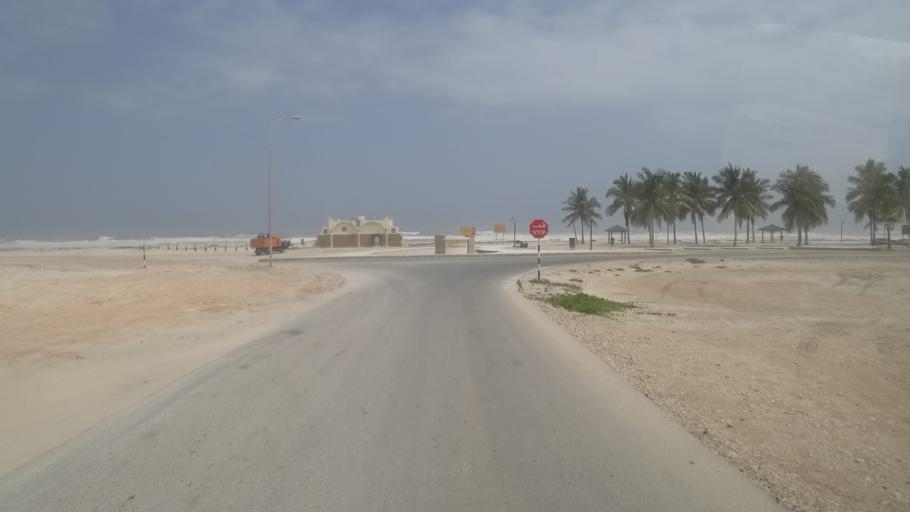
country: OM
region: Zufar
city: Salalah
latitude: 17.0121
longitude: 54.1754
